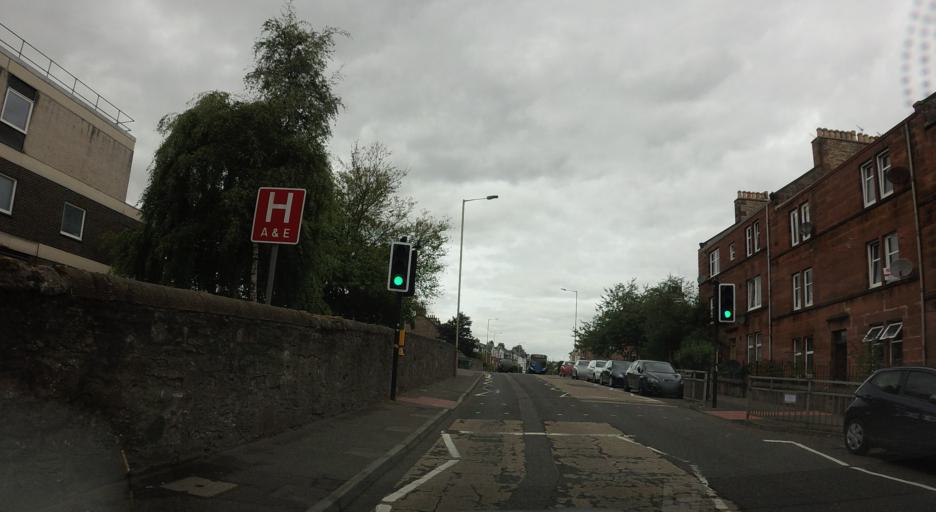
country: GB
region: Scotland
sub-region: Perth and Kinross
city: Perth
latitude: 56.3983
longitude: -3.4545
